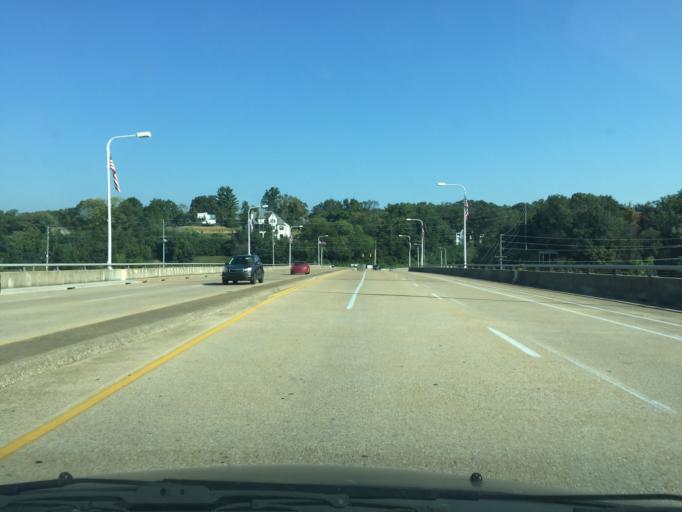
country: US
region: Tennessee
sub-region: Hamilton County
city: Chattanooga
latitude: 35.0589
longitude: -85.3021
